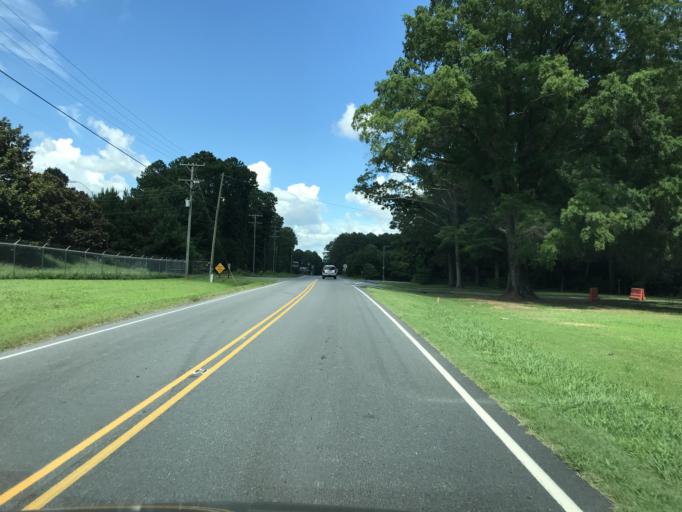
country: US
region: North Carolina
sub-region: Catawba County
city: Lake Norman of Catawba
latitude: 35.5970
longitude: -80.9596
